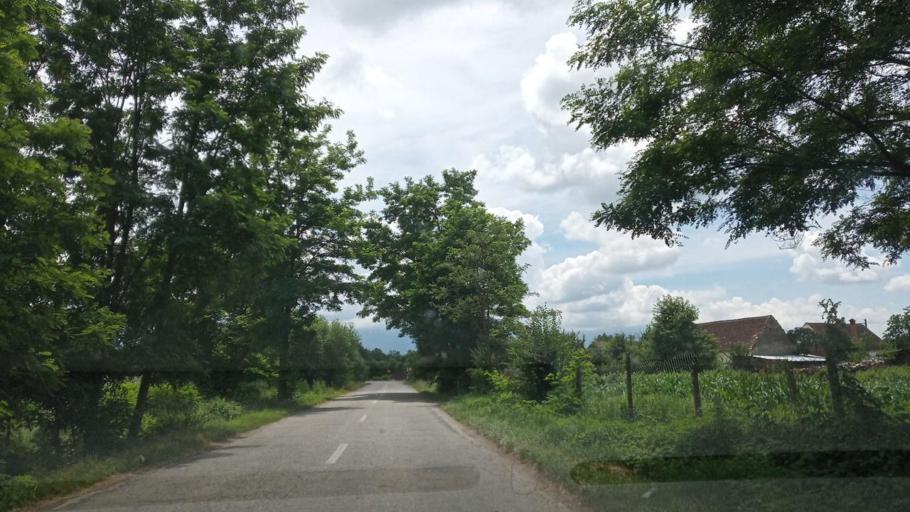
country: RO
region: Sibiu
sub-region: Comuna Porumbacu de Jos
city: Porumbacu de Jos
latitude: 45.7514
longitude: 24.4612
